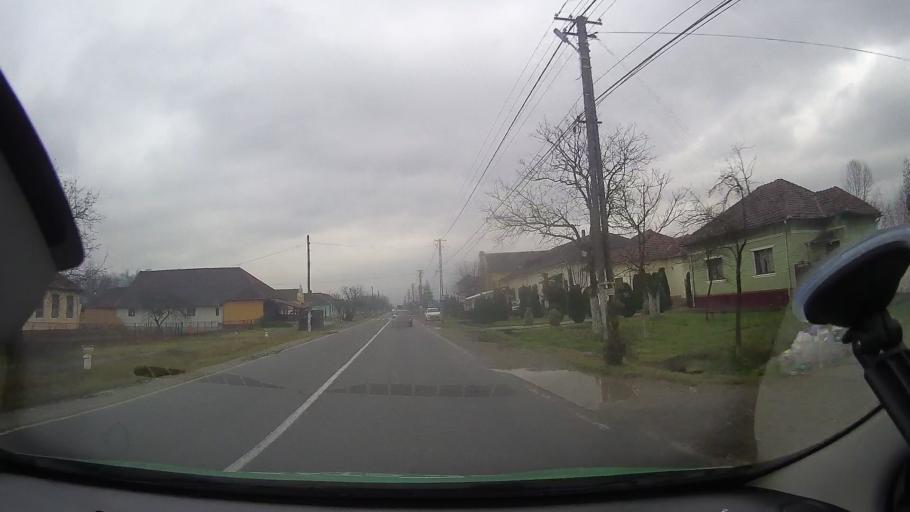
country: RO
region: Arad
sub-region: Comuna Almas
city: Almas
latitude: 46.2835
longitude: 22.2613
